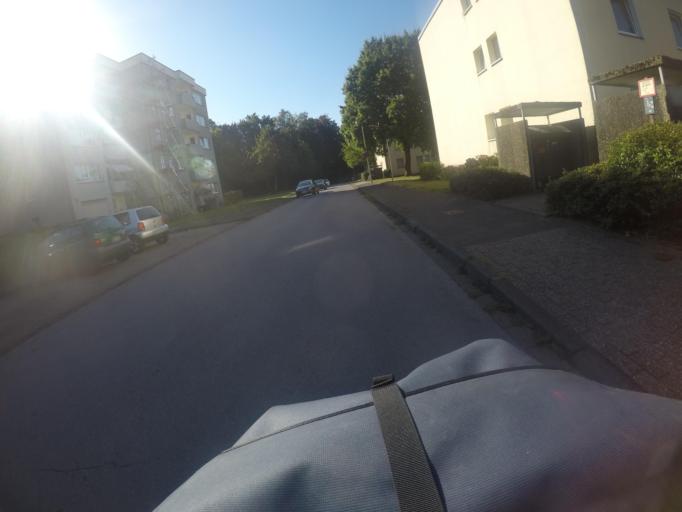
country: DE
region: North Rhine-Westphalia
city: Haan
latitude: 51.1820
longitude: 7.0022
